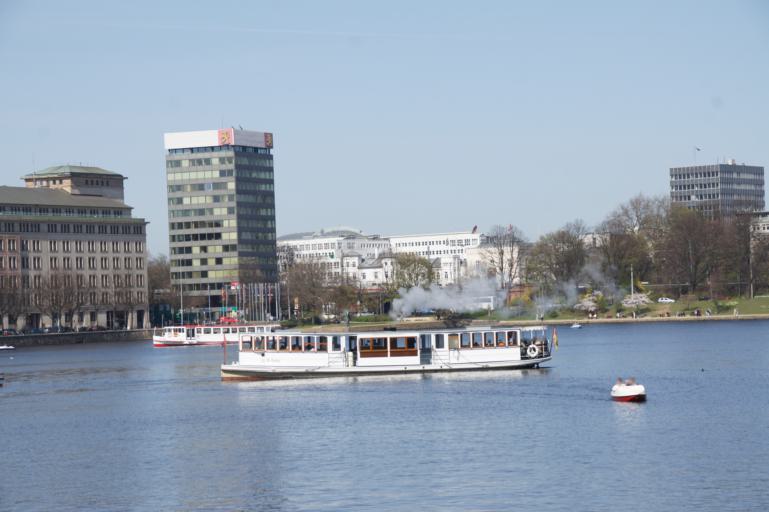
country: DE
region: Hamburg
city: Altstadt
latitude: 53.5529
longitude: 9.9960
